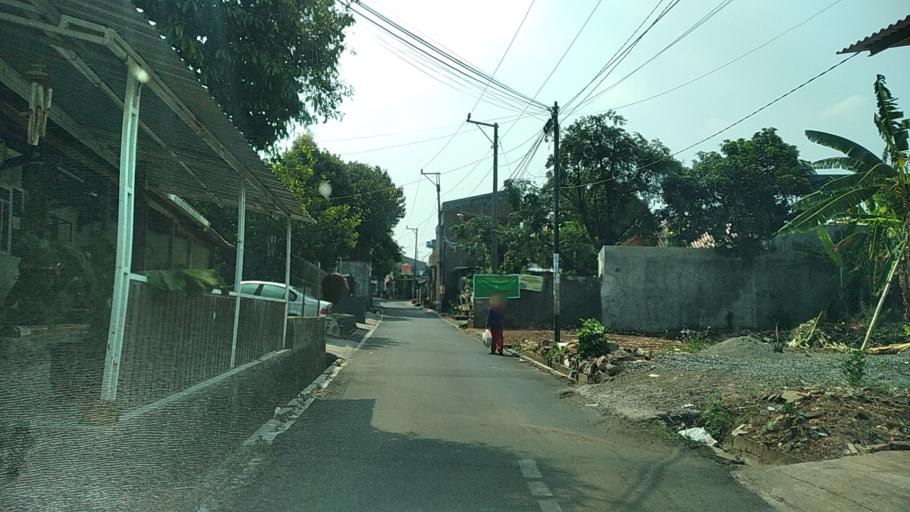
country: ID
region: Central Java
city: Semarang
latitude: -7.0482
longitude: 110.4238
